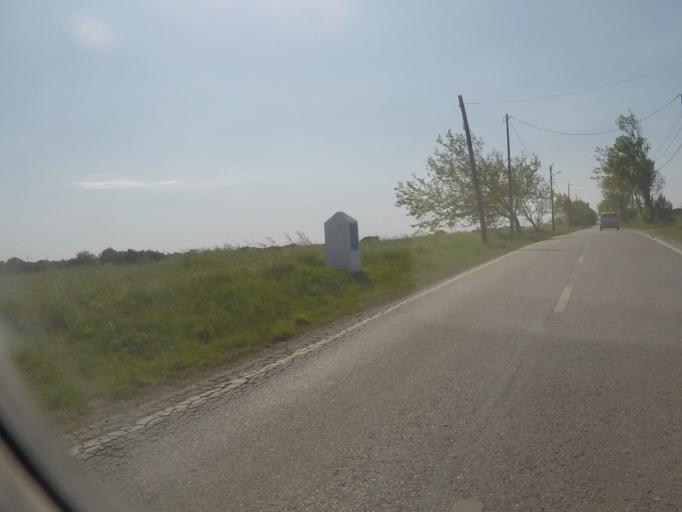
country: PT
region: Setubal
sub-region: Sesimbra
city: Sesimbra
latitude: 38.4436
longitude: -9.1457
